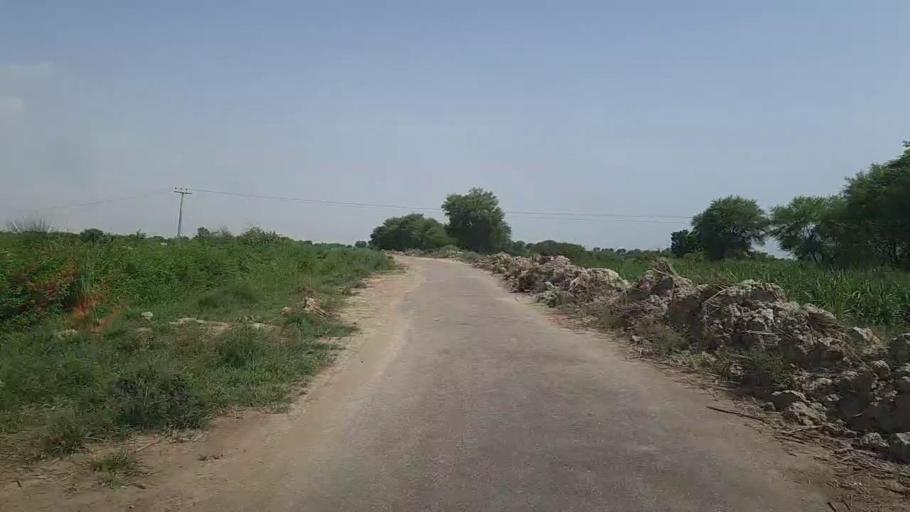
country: PK
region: Sindh
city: Pad Idan
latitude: 26.8127
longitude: 68.3281
